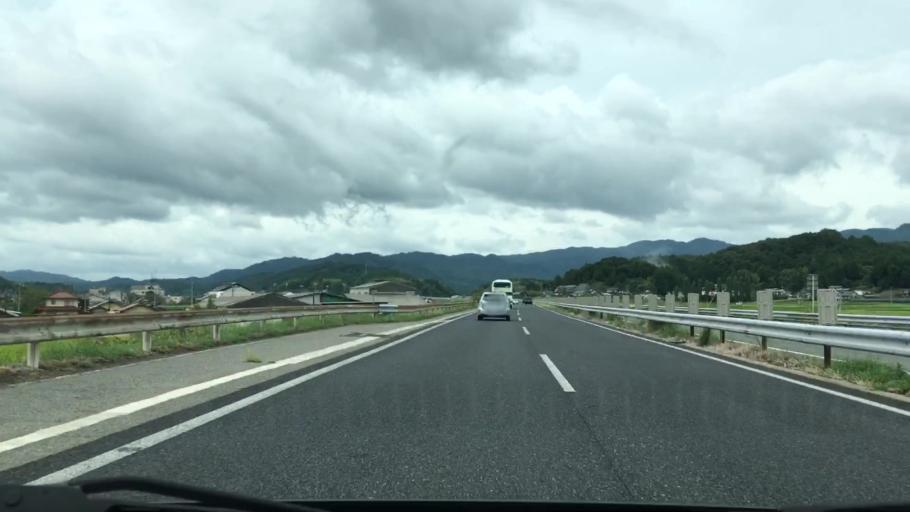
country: JP
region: Okayama
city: Tsuyama
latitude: 35.0585
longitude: 133.9100
